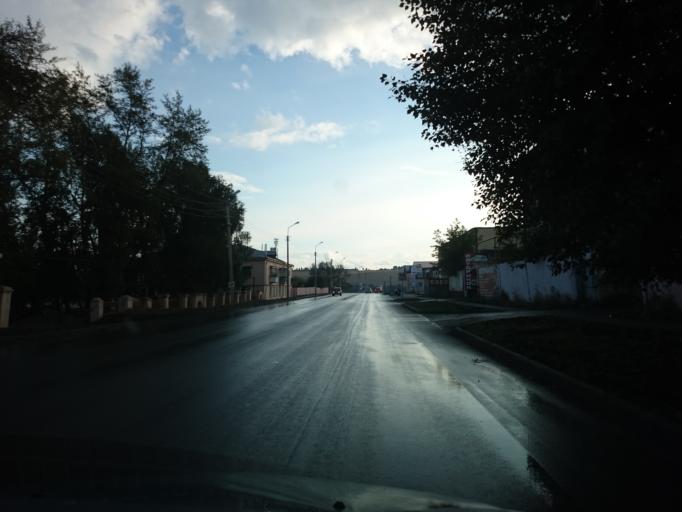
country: RU
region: Bashkortostan
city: Beloretsk
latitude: 53.9576
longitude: 58.3617
